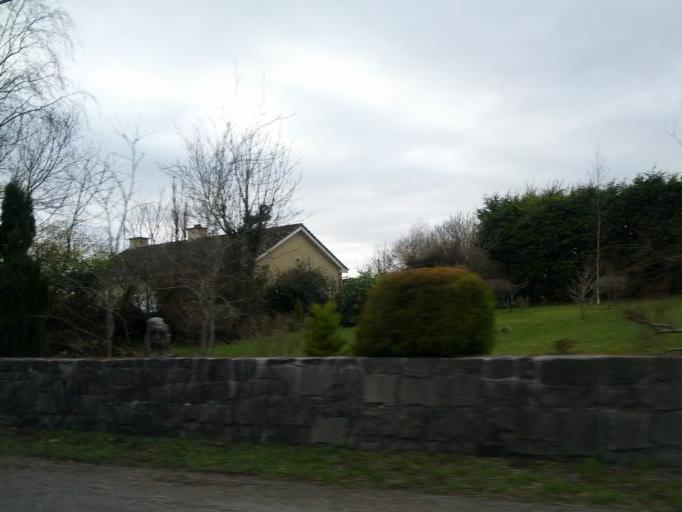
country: IE
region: Connaught
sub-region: County Galway
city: Athenry
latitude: 53.2186
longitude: -8.8097
